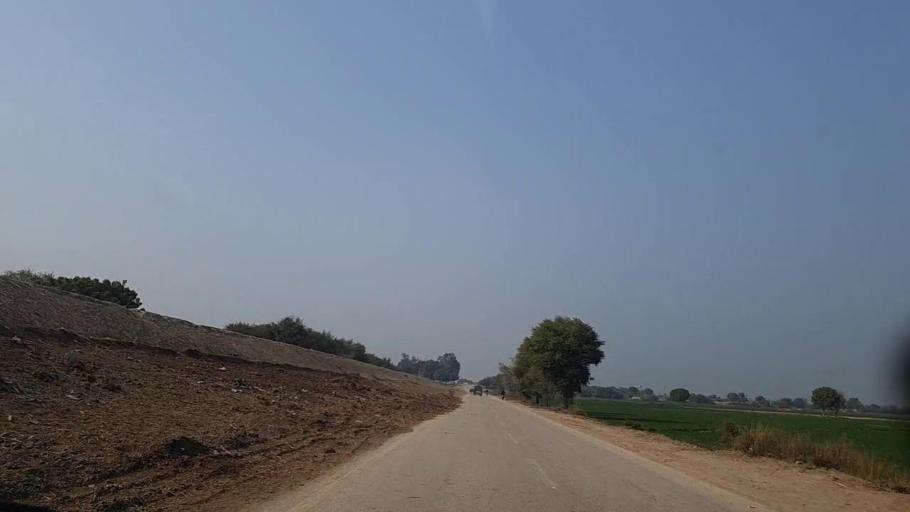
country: PK
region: Sindh
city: Sann
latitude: 26.1639
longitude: 68.1123
